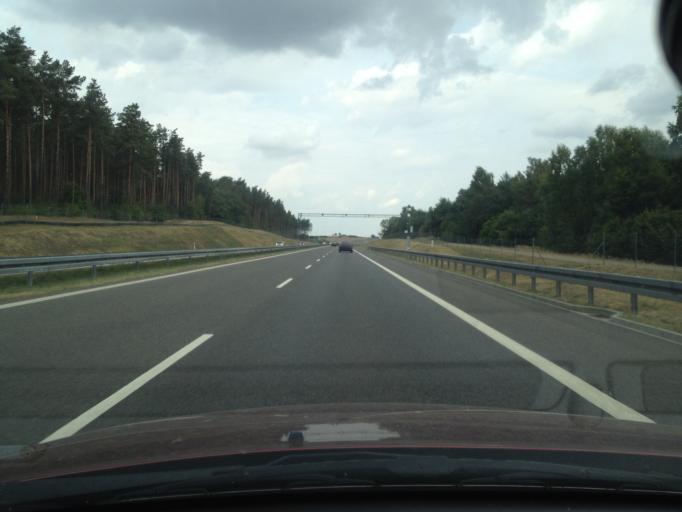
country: PL
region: West Pomeranian Voivodeship
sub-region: Powiat mysliborski
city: Mysliborz
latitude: 53.0146
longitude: 14.8619
